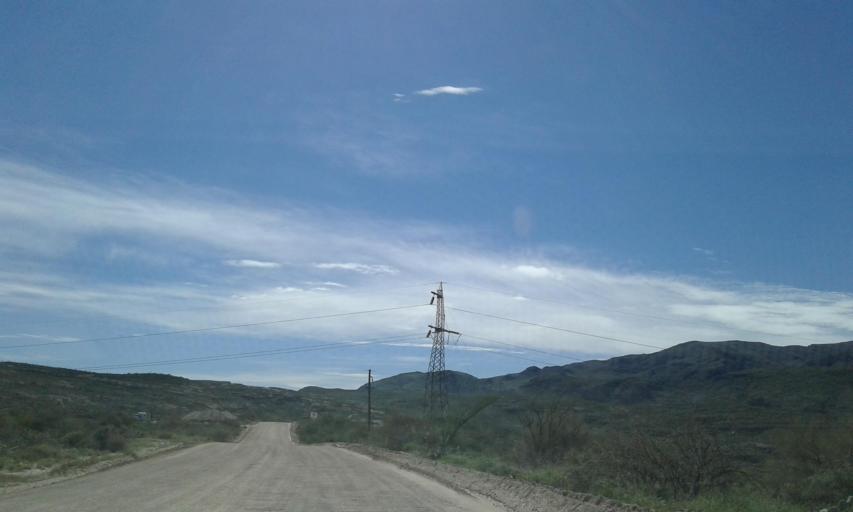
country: US
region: Arizona
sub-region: Pinal County
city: Gold Camp
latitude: 33.5334
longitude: -111.3230
